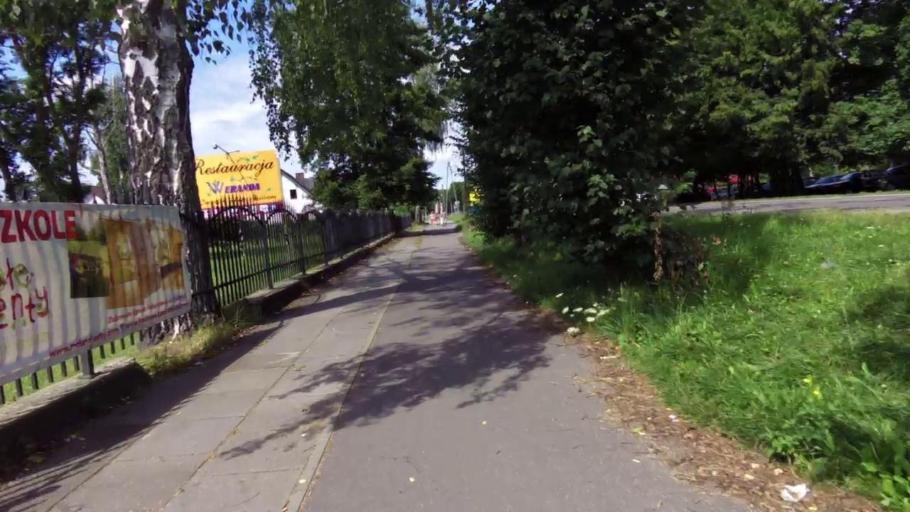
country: PL
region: West Pomeranian Voivodeship
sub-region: Powiat stargardzki
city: Kobylanka
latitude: 53.3525
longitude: 14.9209
